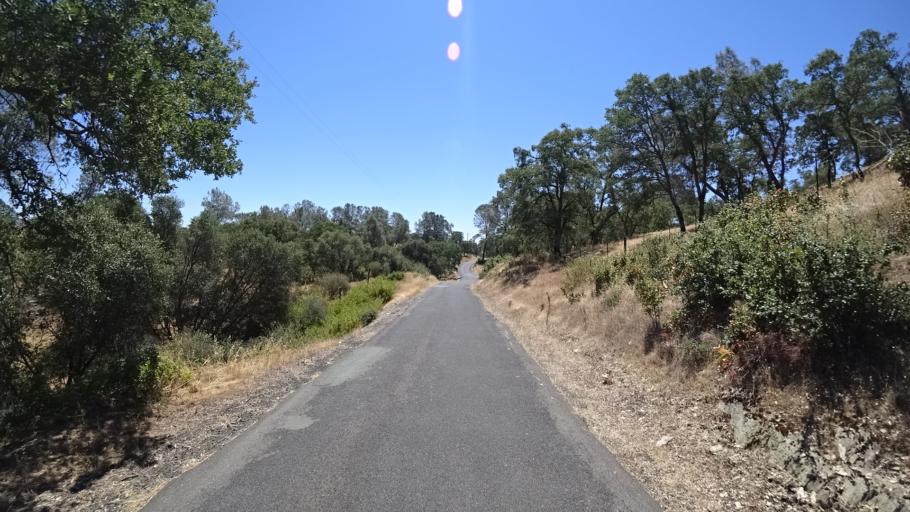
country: US
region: California
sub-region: Calaveras County
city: Copperopolis
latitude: 37.9685
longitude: -120.6922
